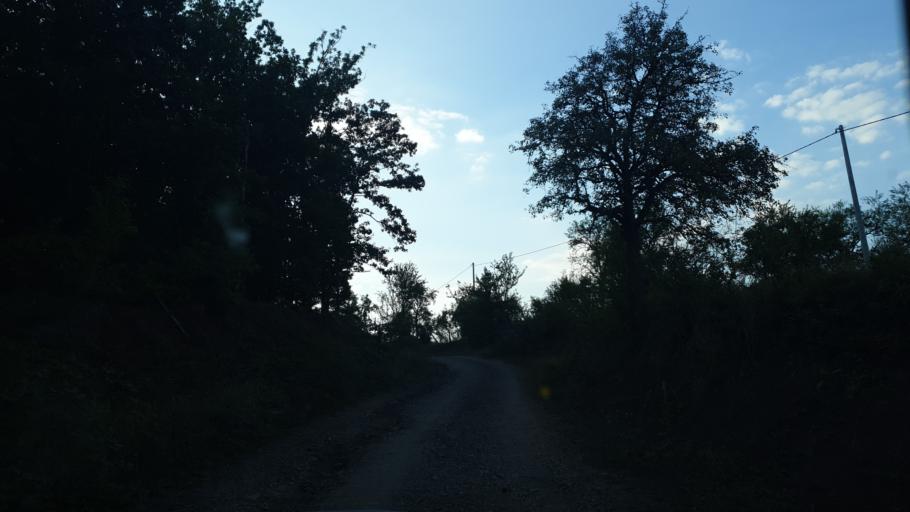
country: RS
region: Central Serbia
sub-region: Zlatiborski Okrug
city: Kosjeric
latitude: 44.0048
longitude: 19.9971
